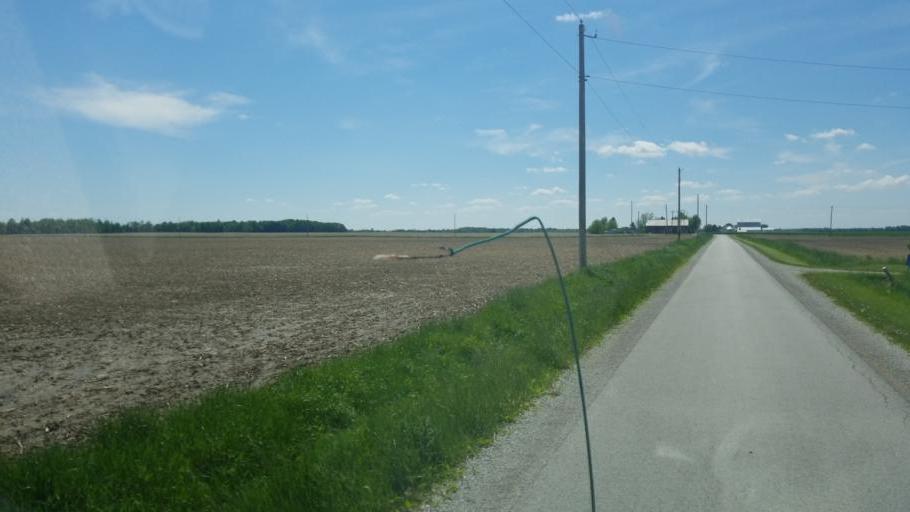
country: US
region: Ohio
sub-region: Crawford County
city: Bucyrus
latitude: 41.0083
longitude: -82.9552
